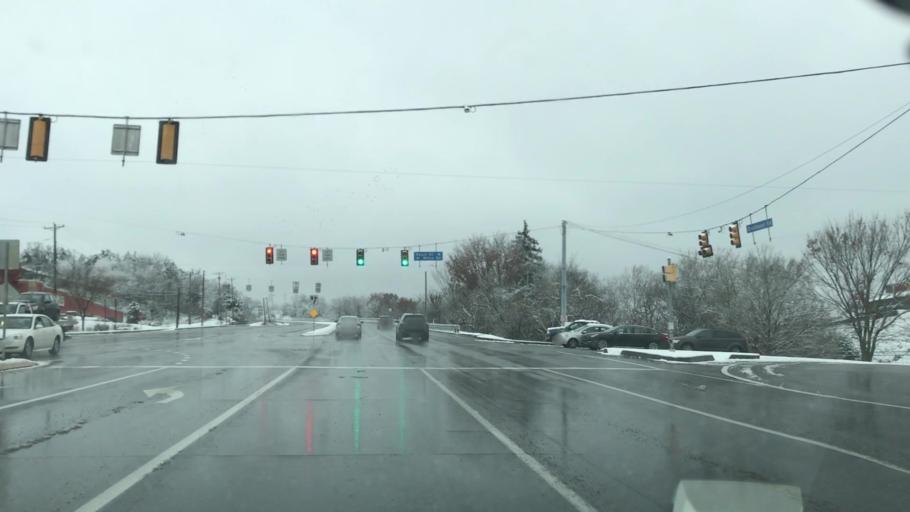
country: US
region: Pennsylvania
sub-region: Beaver County
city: Beaver
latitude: 40.6809
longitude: -80.3026
